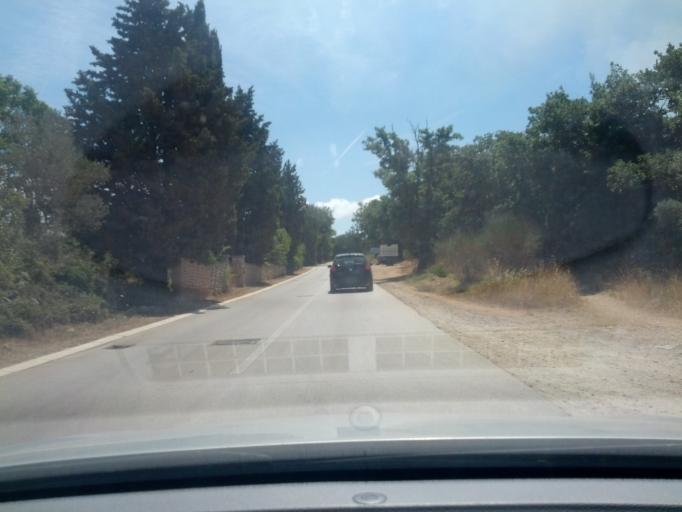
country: HR
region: Istarska
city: Fazana
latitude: 44.9556
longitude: 13.7863
